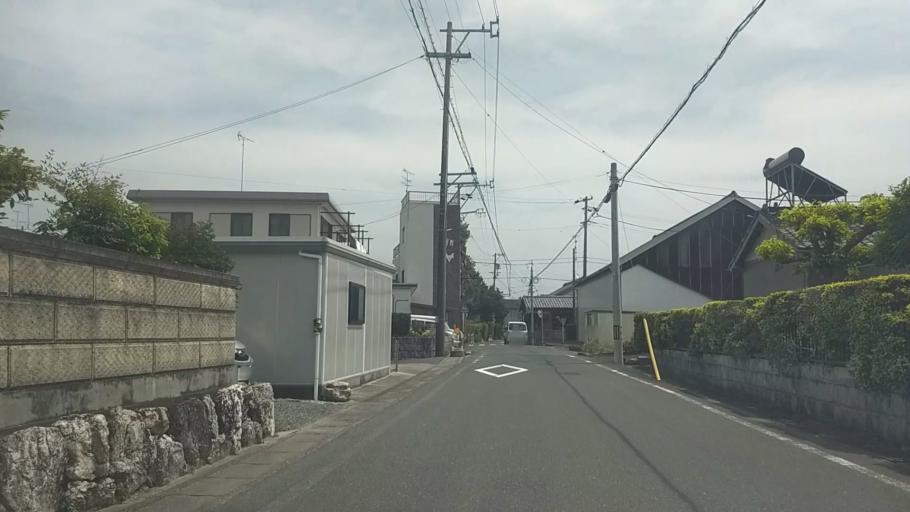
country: JP
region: Shizuoka
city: Kosai-shi
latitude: 34.7340
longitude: 137.5371
